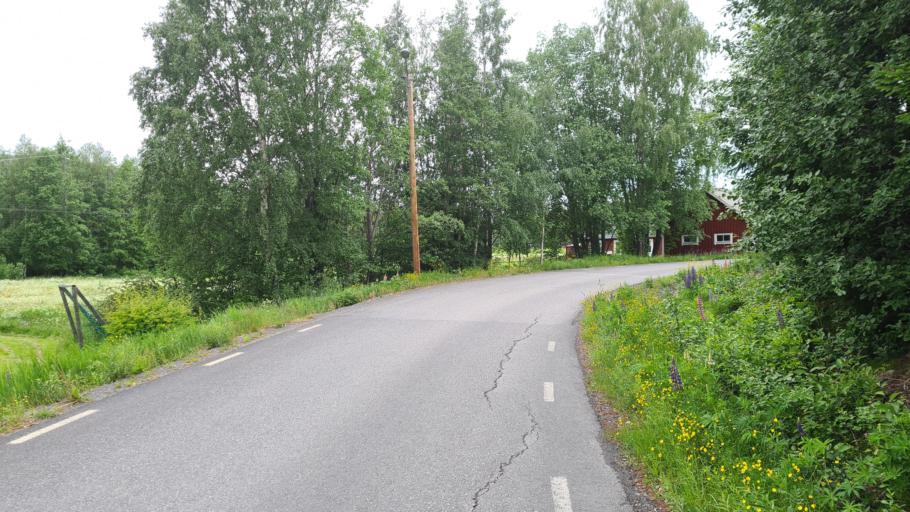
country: SE
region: Vaesternorrland
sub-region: Kramfors Kommun
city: Nordingra
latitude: 62.9746
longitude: 18.4245
